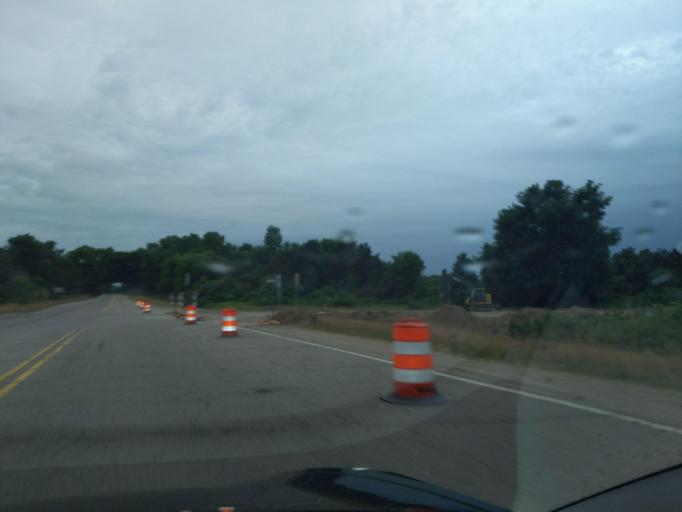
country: US
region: Michigan
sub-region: Clinton County
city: DeWitt
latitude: 42.8059
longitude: -84.6027
